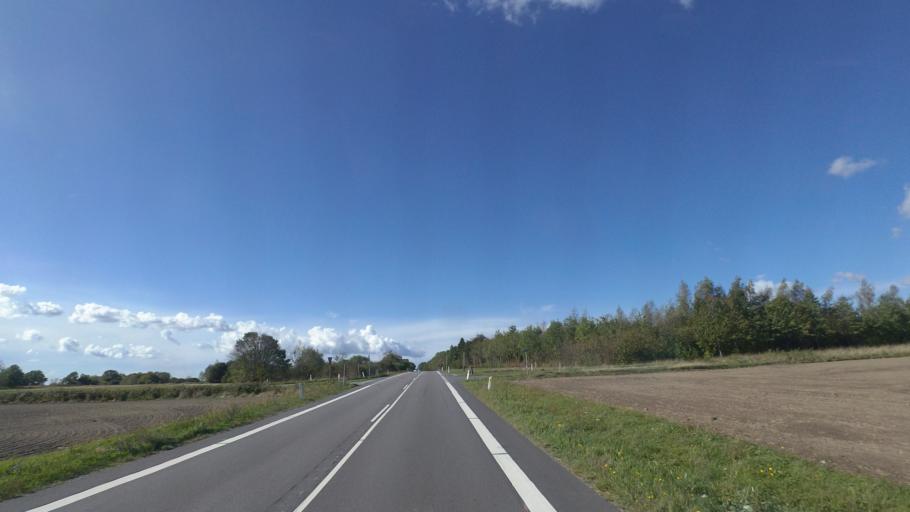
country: DK
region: Capital Region
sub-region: Bornholm Kommune
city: Akirkeby
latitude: 55.0672
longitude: 14.9998
